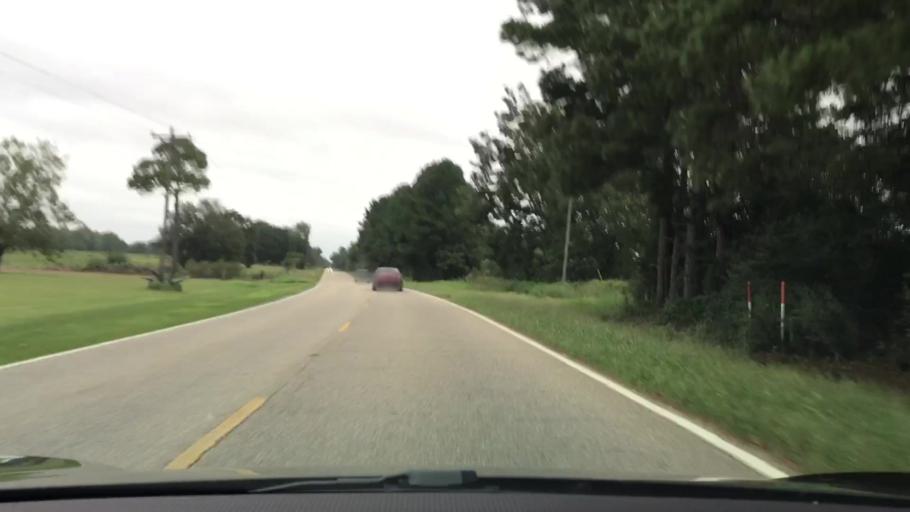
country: US
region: Alabama
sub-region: Geneva County
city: Samson
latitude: 31.1607
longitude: -86.1417
